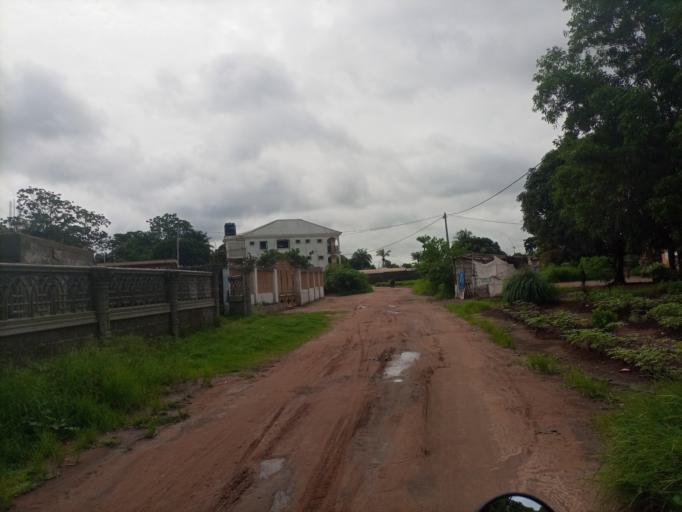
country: SL
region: Northern Province
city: Sawkta
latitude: 8.6243
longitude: -13.2012
